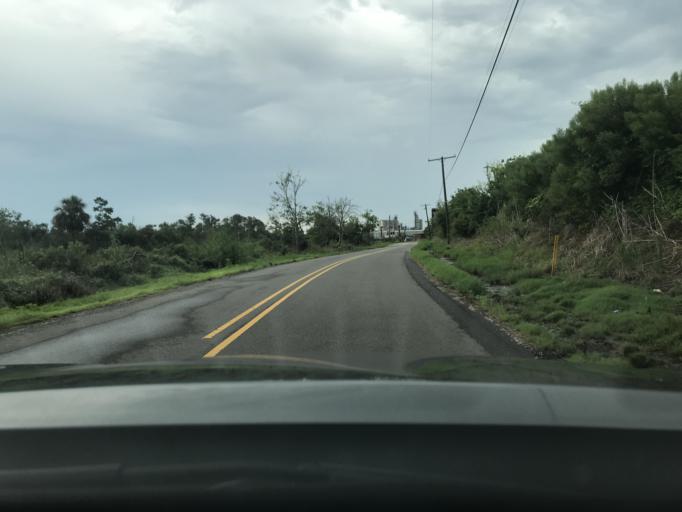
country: US
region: Louisiana
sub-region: Calcasieu Parish
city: Westlake
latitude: 30.2247
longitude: -93.2509
